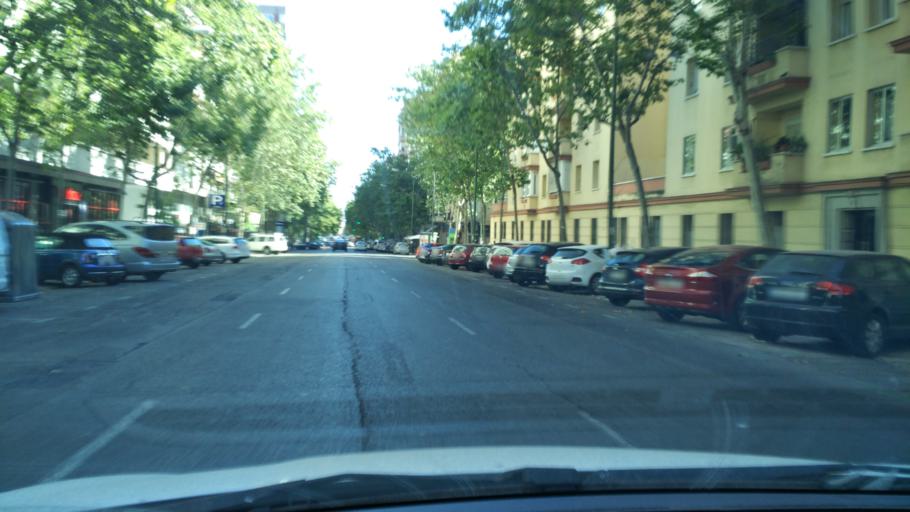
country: ES
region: Madrid
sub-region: Provincia de Madrid
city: Chamartin
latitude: 40.4548
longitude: -3.6948
